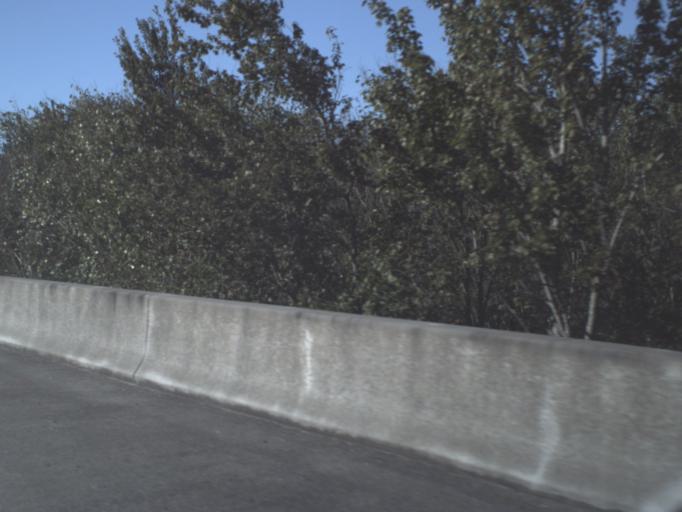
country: US
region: Florida
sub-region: Seminole County
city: Oviedo
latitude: 28.6676
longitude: -81.2278
